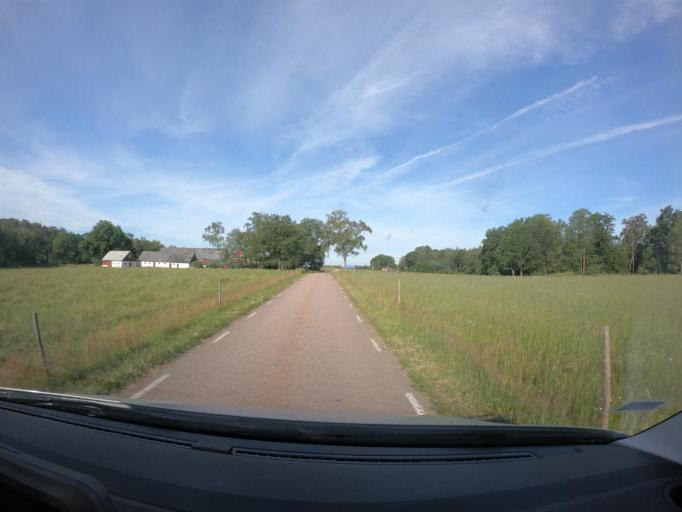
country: SE
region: Skane
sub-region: Angelholms Kommun
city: Munka-Ljungby
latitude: 56.3441
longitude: 13.0060
